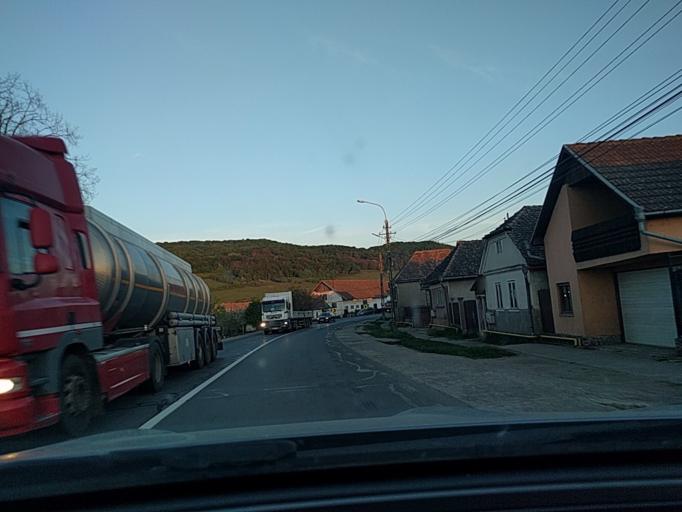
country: RO
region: Mures
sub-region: Comuna Balauseri
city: Chendu
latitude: 46.3918
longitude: 24.7286
